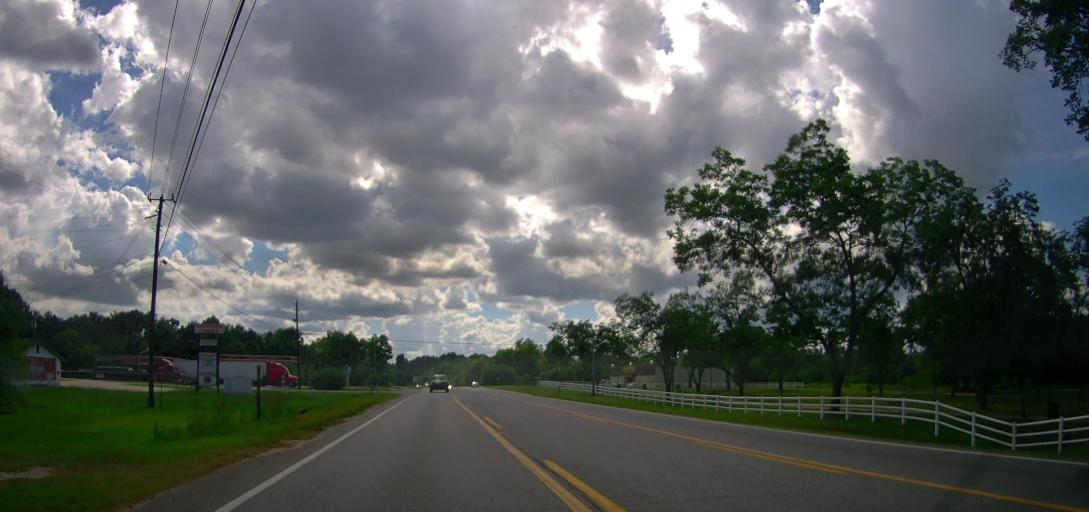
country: US
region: Alabama
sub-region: Russell County
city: Ladonia
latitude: 32.4566
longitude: -85.1921
